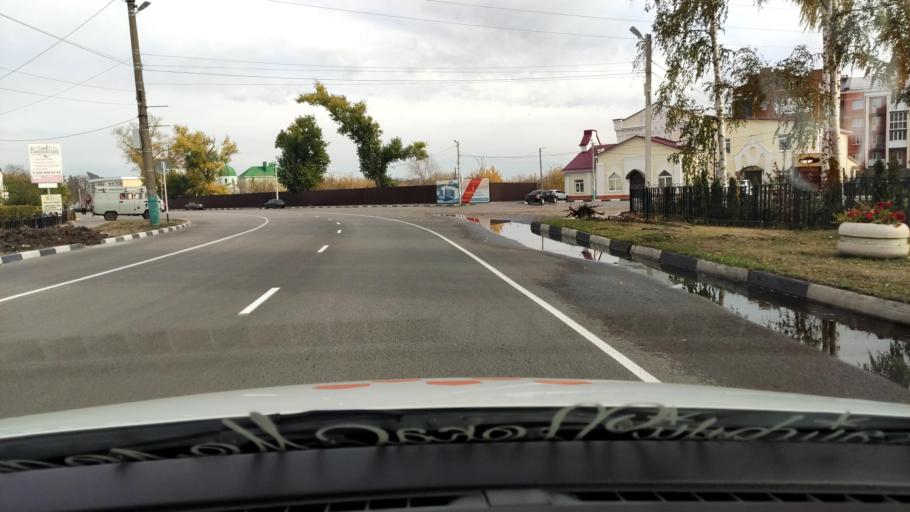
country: RU
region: Voronezj
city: Ramon'
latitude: 51.9101
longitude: 39.3377
